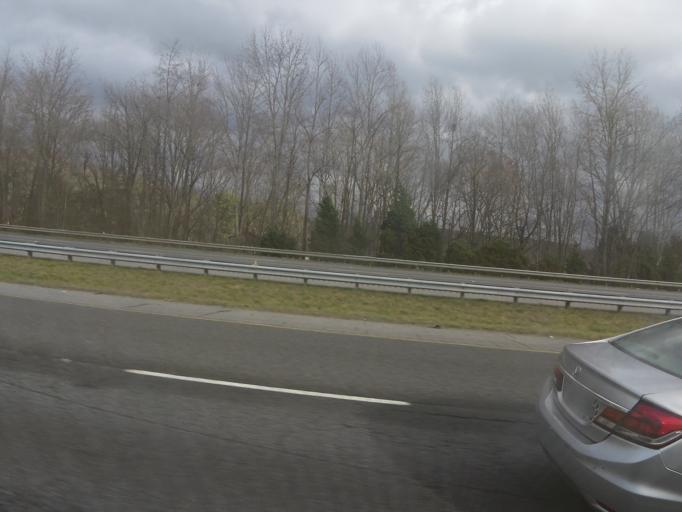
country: US
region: Georgia
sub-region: Whitfield County
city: Dalton
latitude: 34.7234
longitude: -85.0071
